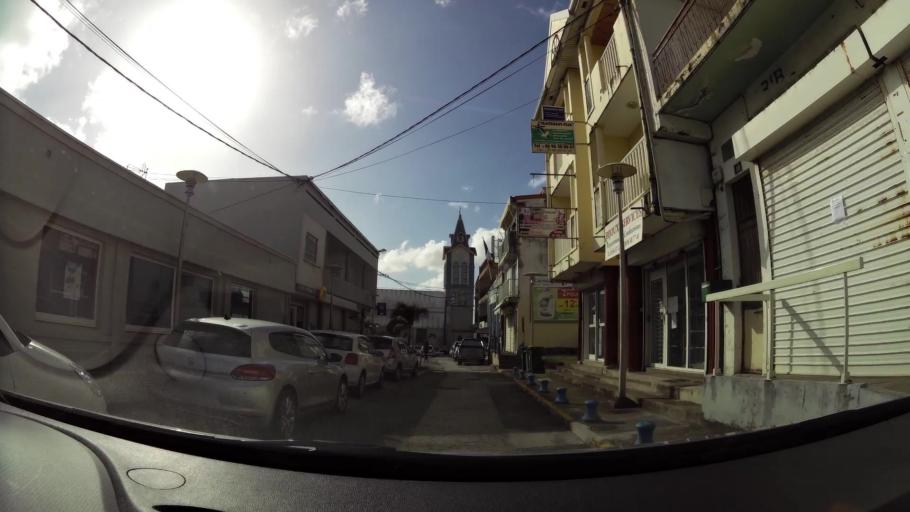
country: MQ
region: Martinique
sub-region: Martinique
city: Le Robert
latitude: 14.6778
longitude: -60.9393
